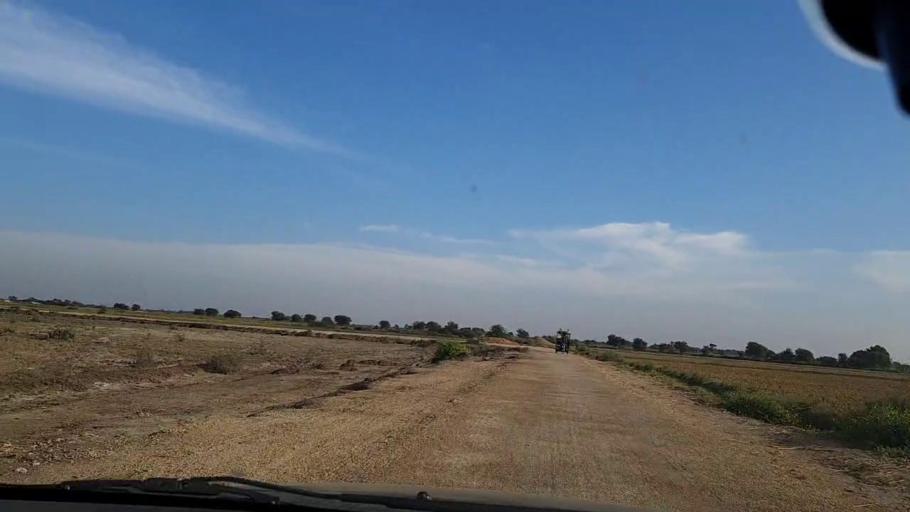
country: PK
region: Sindh
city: Mirpur Batoro
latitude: 24.6578
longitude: 68.3024
